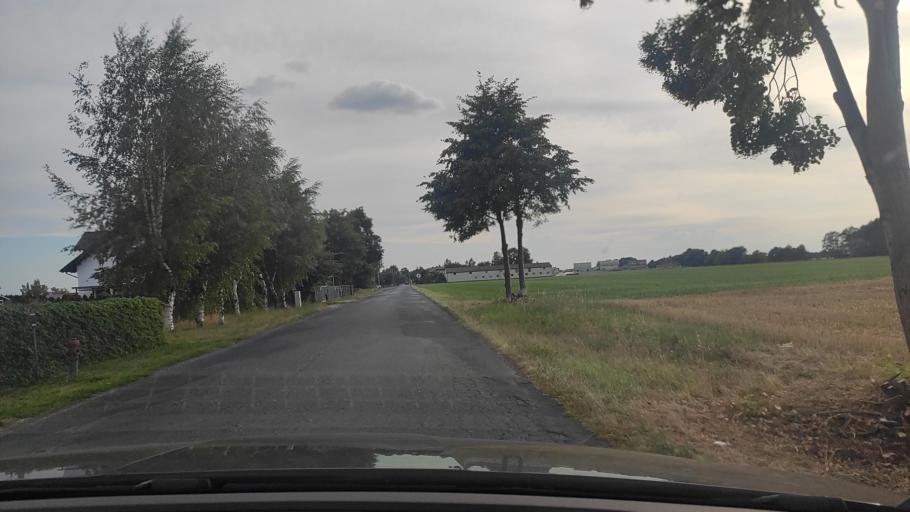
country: PL
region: Greater Poland Voivodeship
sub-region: Powiat poznanski
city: Kleszczewo
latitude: 52.3744
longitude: 17.1585
